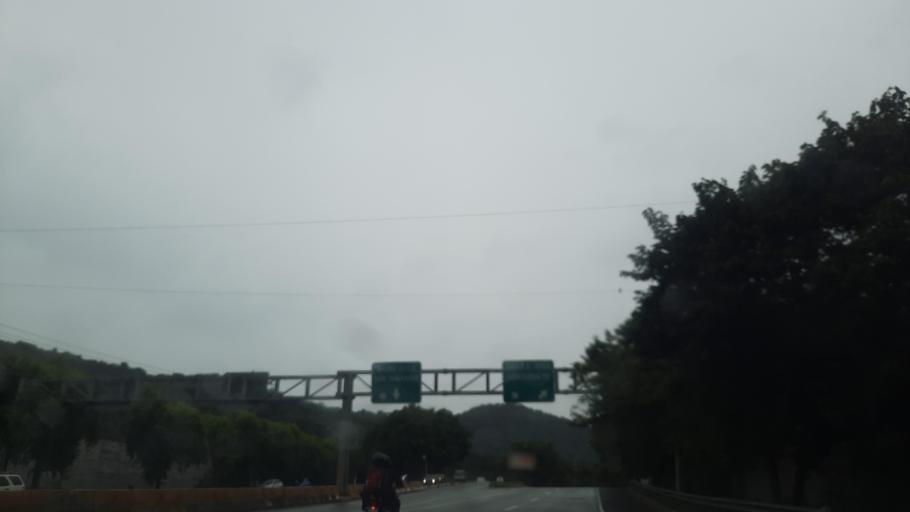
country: SV
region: La Libertad
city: Santa Tecla
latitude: 13.6774
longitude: -89.3026
